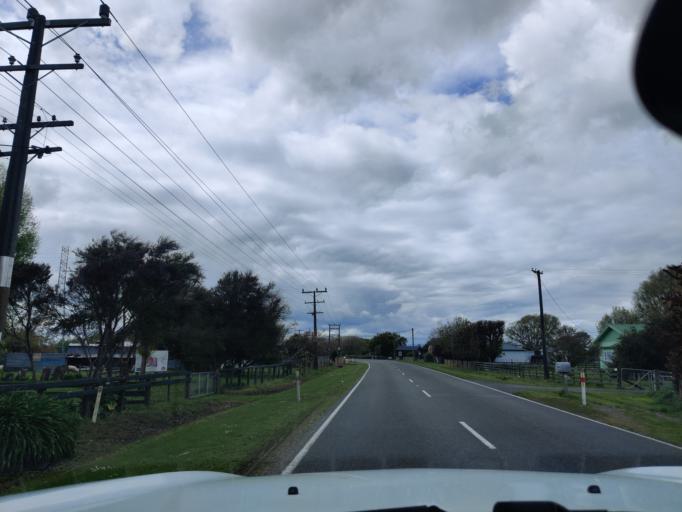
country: NZ
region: Manawatu-Wanganui
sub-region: Palmerston North City
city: Palmerston North
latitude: -40.2444
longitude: 175.5530
